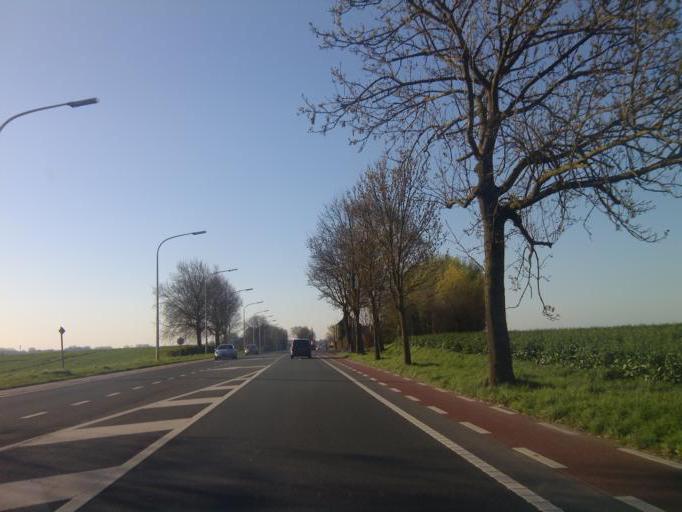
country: BE
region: Wallonia
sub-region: Province du Brabant Wallon
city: Louvain-la-Neuve
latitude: 50.6514
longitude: 4.6404
